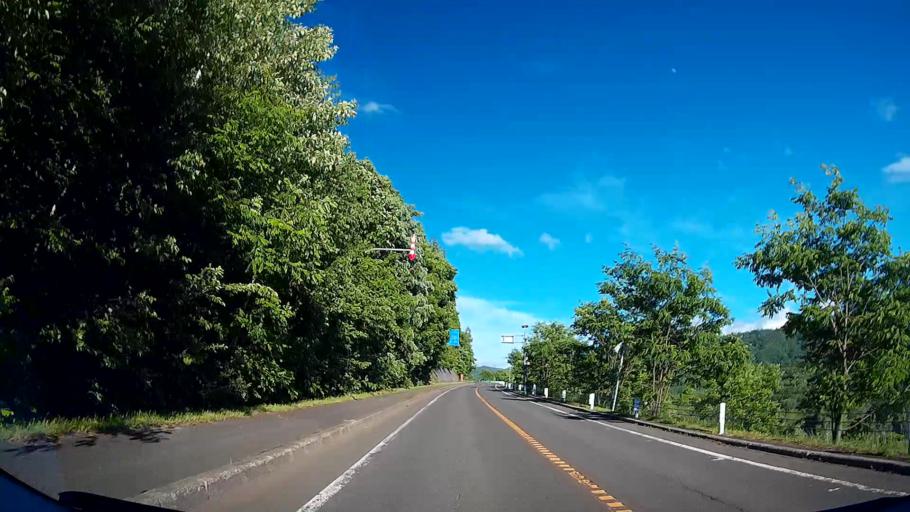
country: JP
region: Hokkaido
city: Sapporo
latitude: 42.9788
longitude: 141.1380
